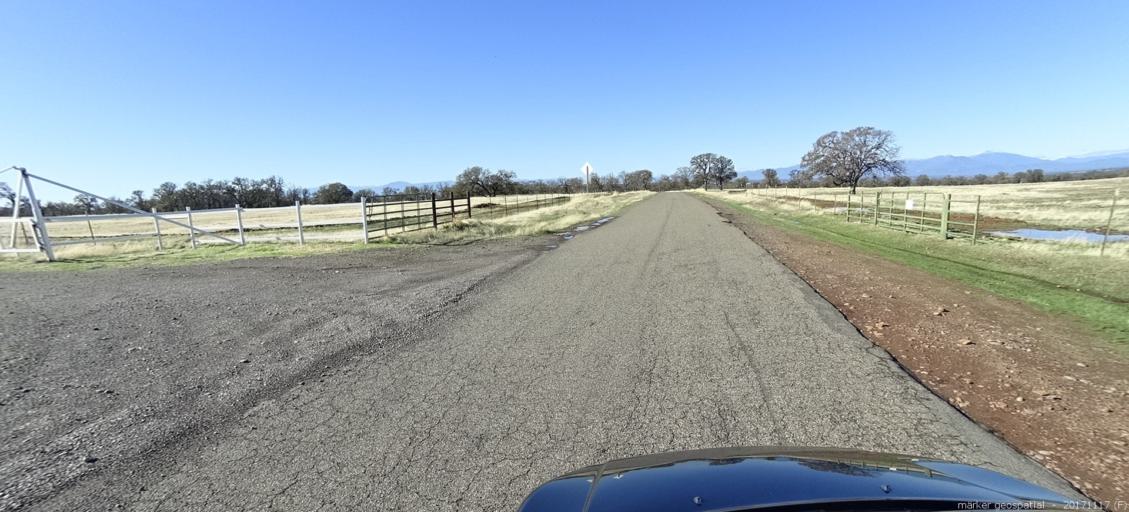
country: US
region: California
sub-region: Shasta County
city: Cottonwood
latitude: 40.4257
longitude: -122.1701
